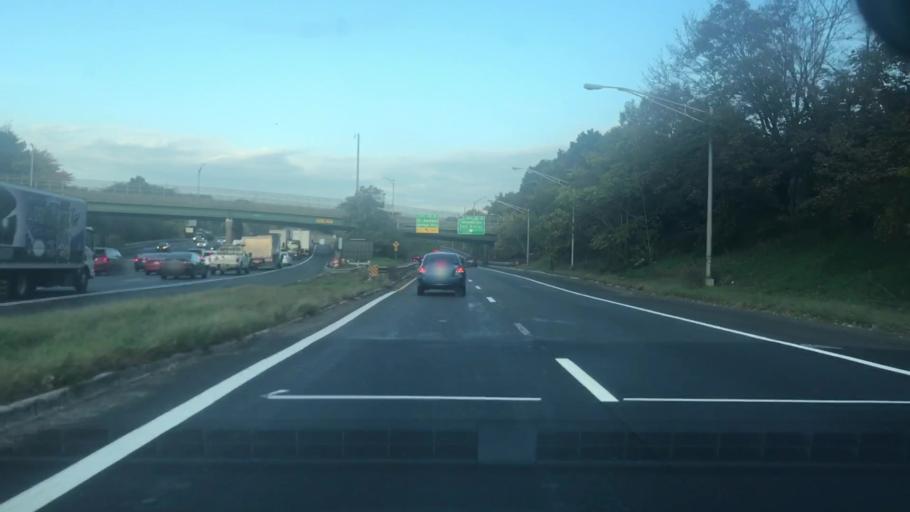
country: US
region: New Jersey
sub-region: Essex County
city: East Orange
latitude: 40.7571
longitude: -74.2021
